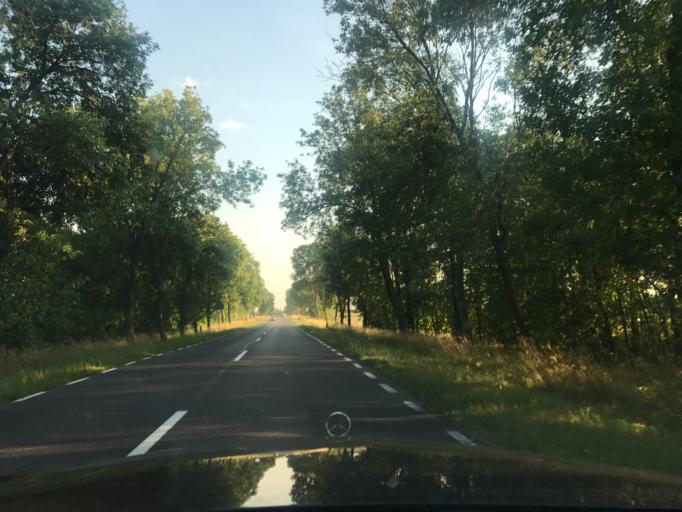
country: PL
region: Lublin Voivodeship
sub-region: Powiat parczewski
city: Debowa Kloda
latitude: 51.6603
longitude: 23.0049
